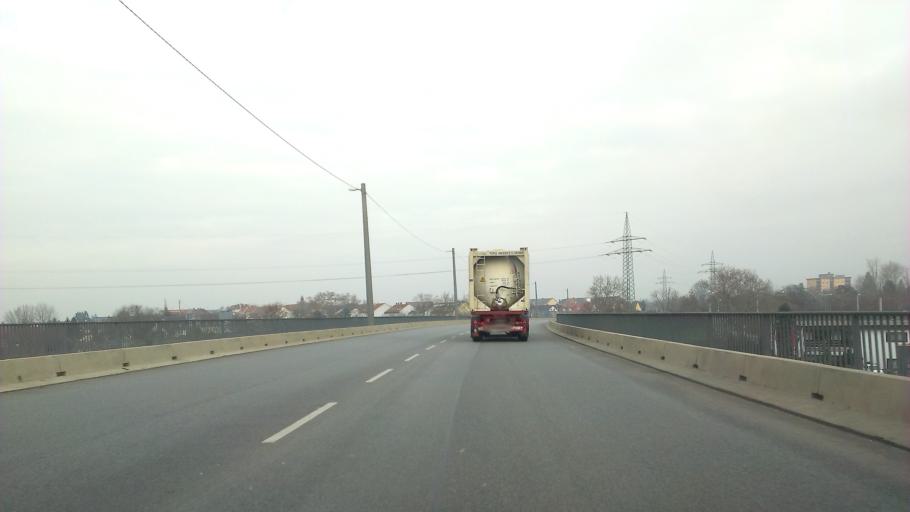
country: DE
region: Baden-Wuerttemberg
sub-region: Karlsruhe Region
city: Mannheim
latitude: 49.5347
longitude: 8.4516
